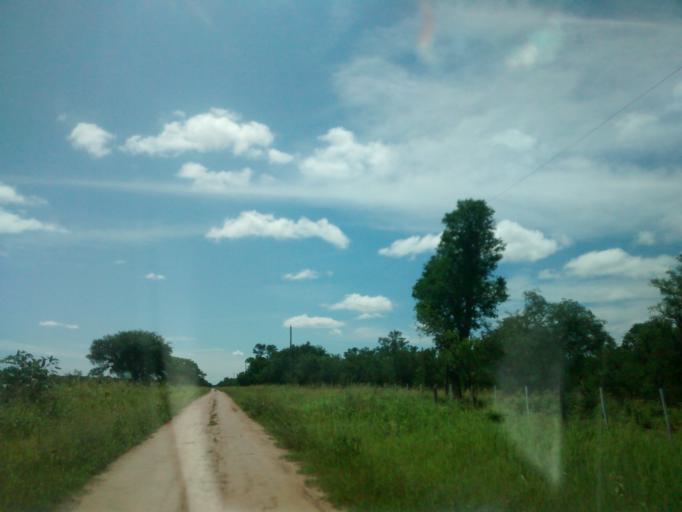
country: AR
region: Chaco
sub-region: Departamento de Quitilipi
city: Quitilipi
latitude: -26.7824
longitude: -60.2263
